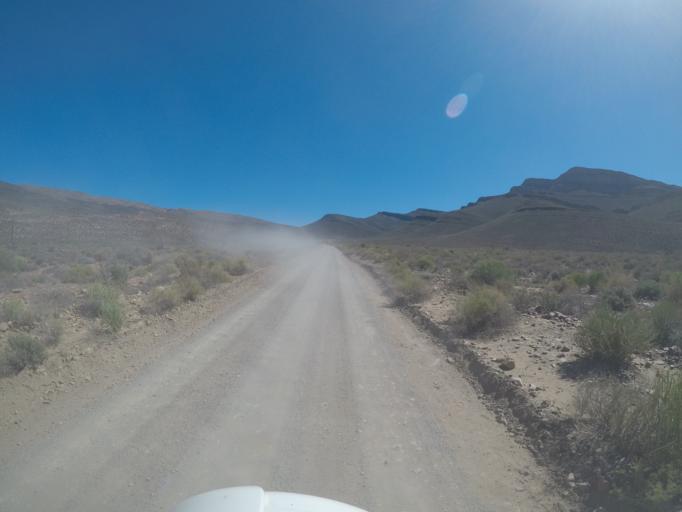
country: ZA
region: Western Cape
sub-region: West Coast District Municipality
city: Clanwilliam
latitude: -32.6350
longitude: 19.3994
